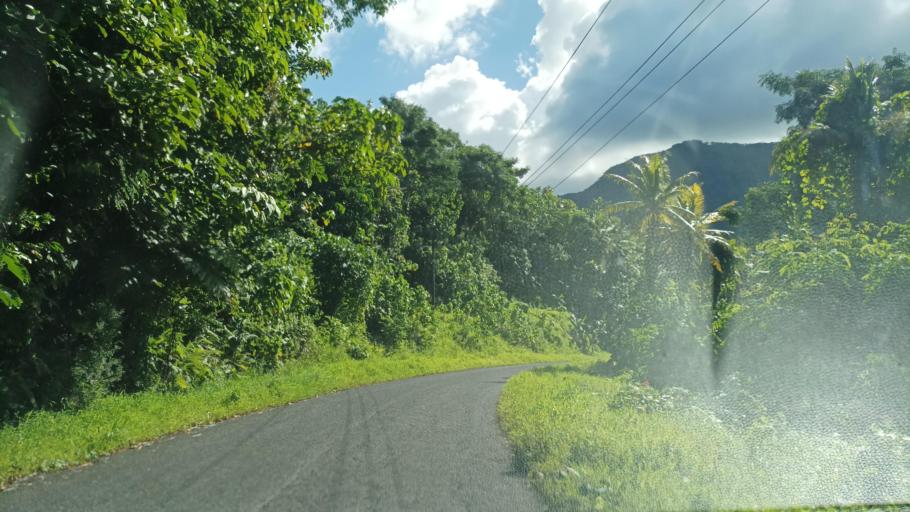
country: FM
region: Pohnpei
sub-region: Kolonia Municipality
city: Kolonia
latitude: 6.9244
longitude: 158.2841
